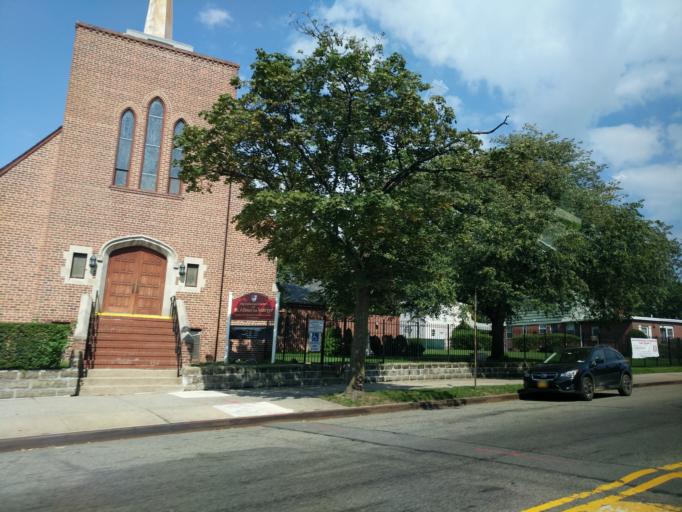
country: US
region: New York
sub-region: Queens County
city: Jamaica
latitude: 40.6924
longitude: -73.7624
